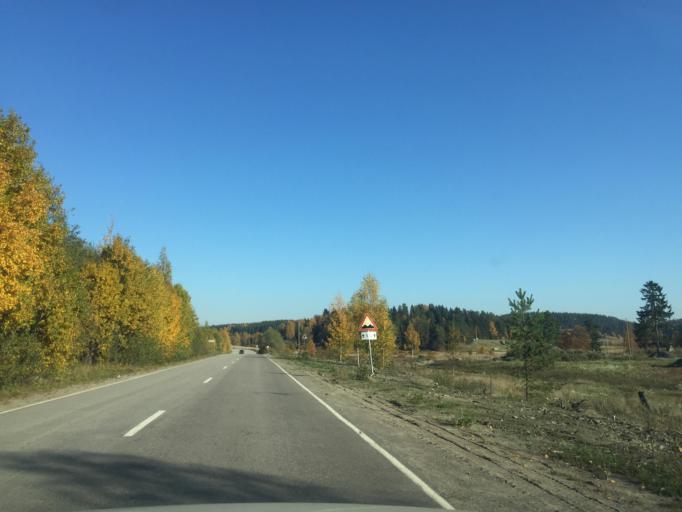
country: RU
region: Leningrad
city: Kuznechnoye
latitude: 61.3044
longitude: 29.9236
